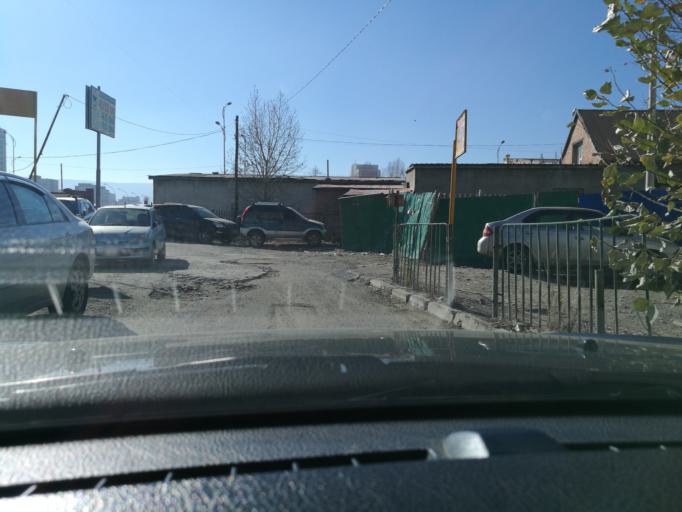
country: MN
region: Ulaanbaatar
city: Ulaanbaatar
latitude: 47.9303
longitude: 106.9302
